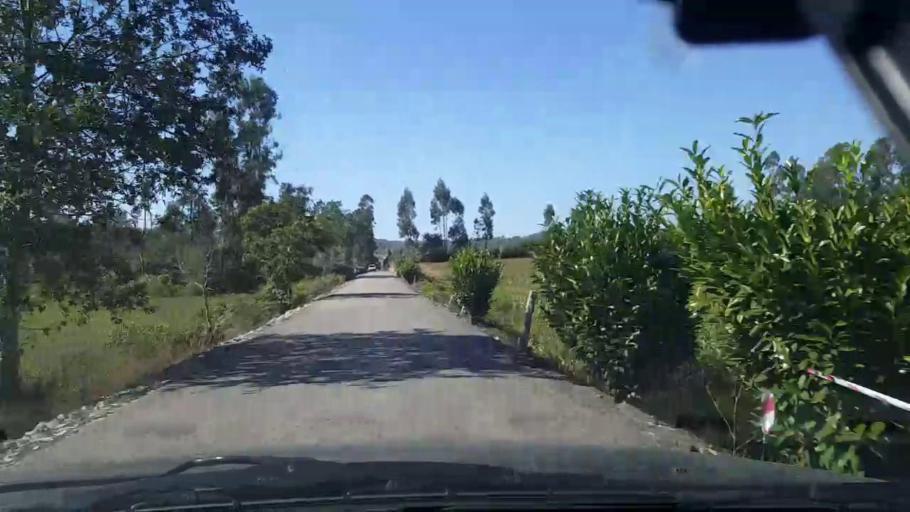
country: PT
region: Braga
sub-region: Vila Nova de Famalicao
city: Ribeirao
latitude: 41.3558
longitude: -8.6389
